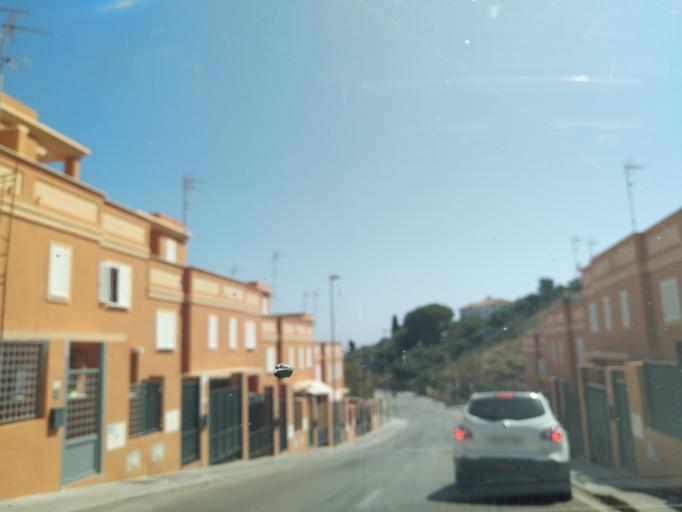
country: ES
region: Andalusia
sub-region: Provincia de Malaga
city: Valdes
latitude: 36.7203
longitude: -4.1991
